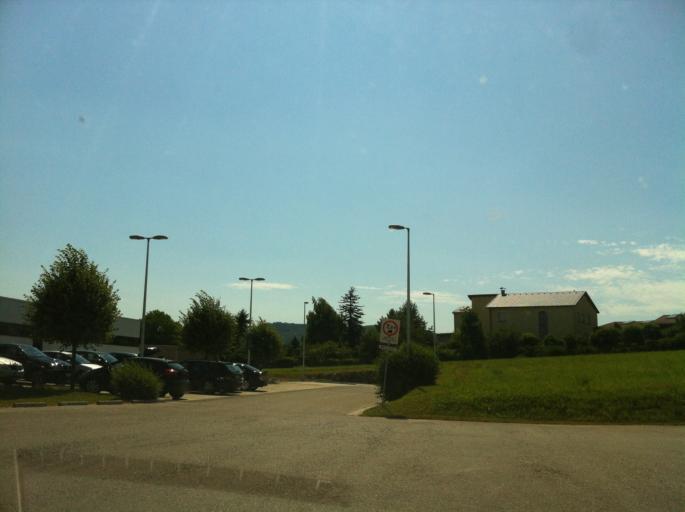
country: AT
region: Lower Austria
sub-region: Politischer Bezirk Tulln
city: Sieghartskirchen
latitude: 48.2557
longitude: 16.0080
